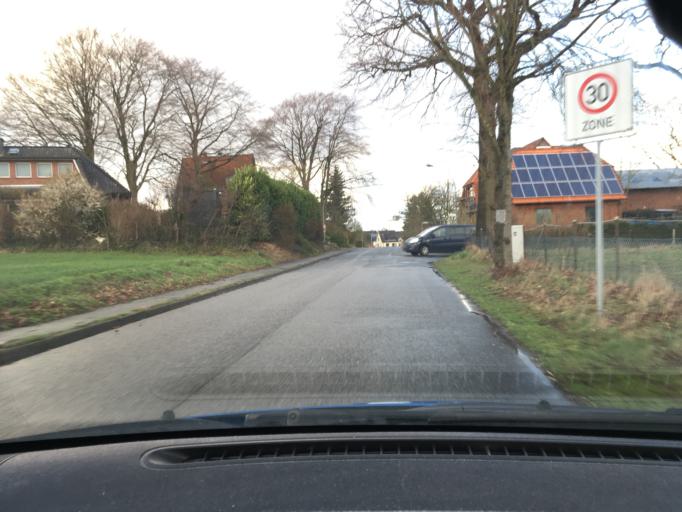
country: DE
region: Lower Saxony
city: Harmstorf
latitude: 53.3737
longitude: 9.9865
